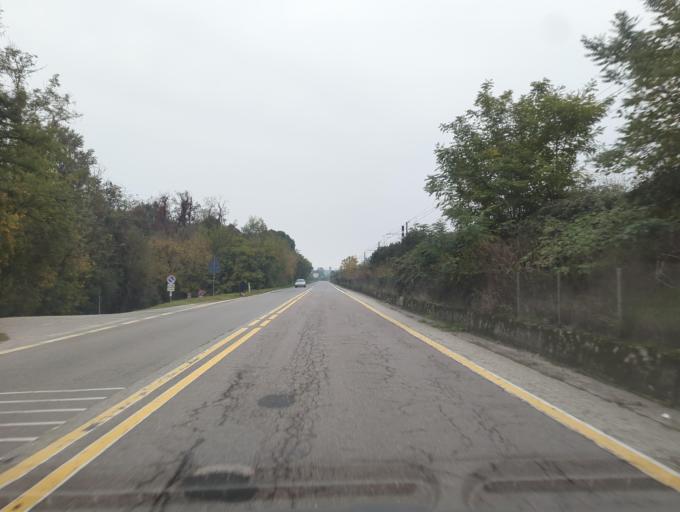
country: IT
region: Lombardy
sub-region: Citta metropolitana di Milano
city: Turbigo
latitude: 45.5109
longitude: 8.7218
